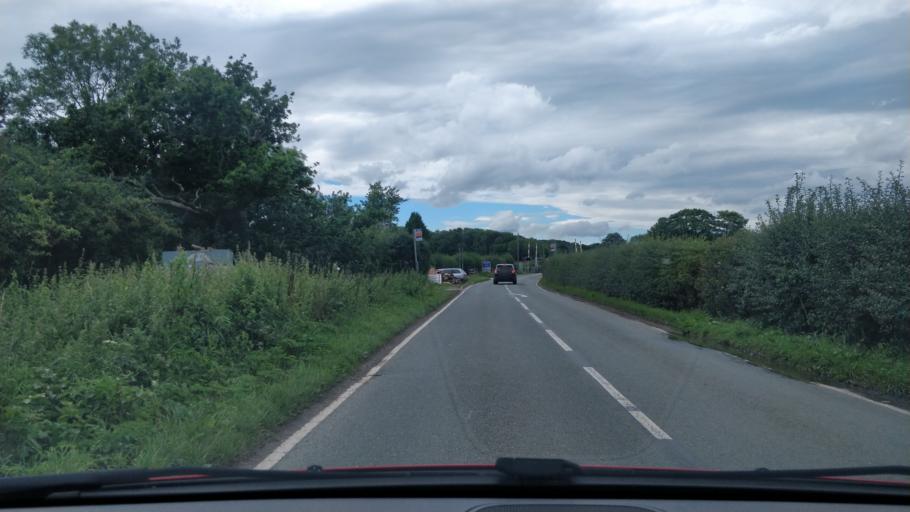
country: GB
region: Wales
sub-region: Wrexham
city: Rossett
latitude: 53.1541
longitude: -2.9333
